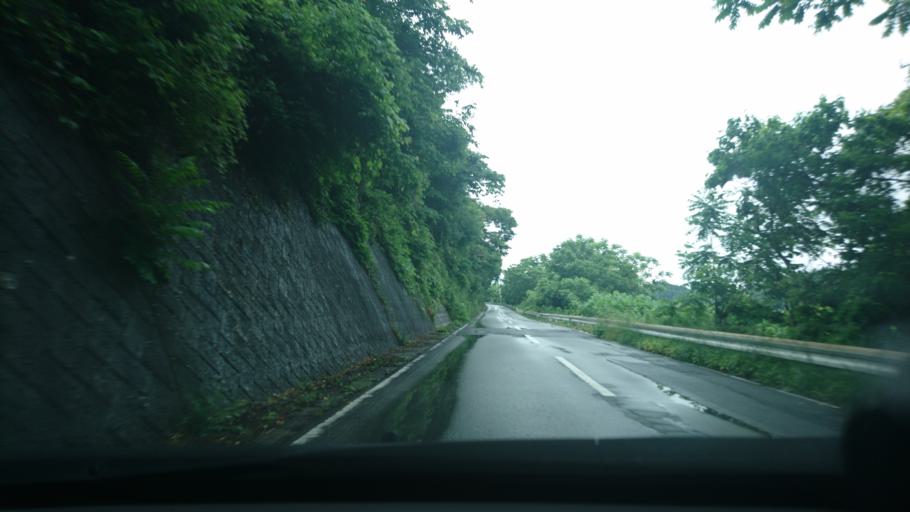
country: JP
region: Miyagi
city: Wakuya
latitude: 38.6766
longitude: 141.2837
